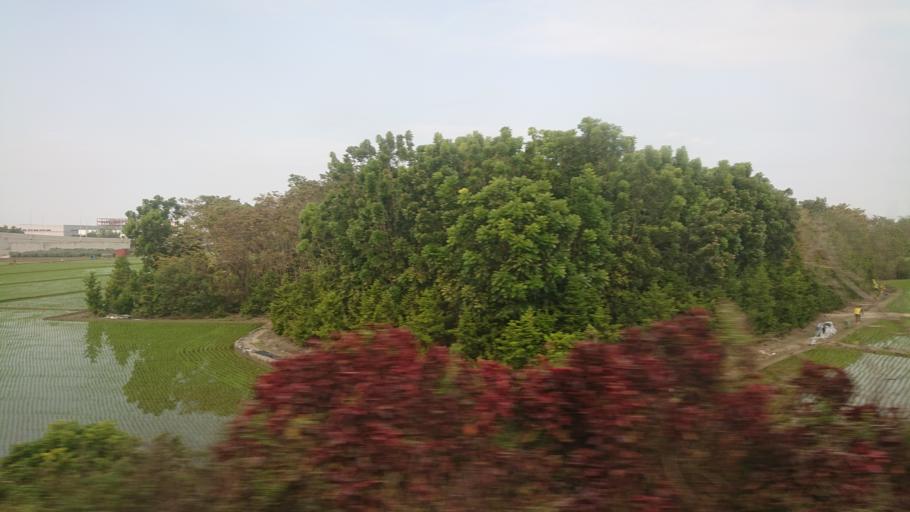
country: TW
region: Taiwan
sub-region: Yunlin
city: Douliu
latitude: 23.7253
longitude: 120.5734
